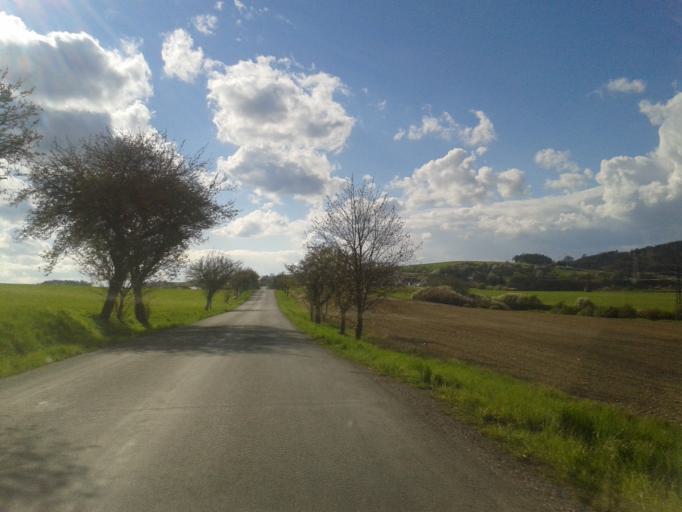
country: CZ
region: Central Bohemia
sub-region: Okres Beroun
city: Lodenice
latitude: 50.0100
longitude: 14.1285
